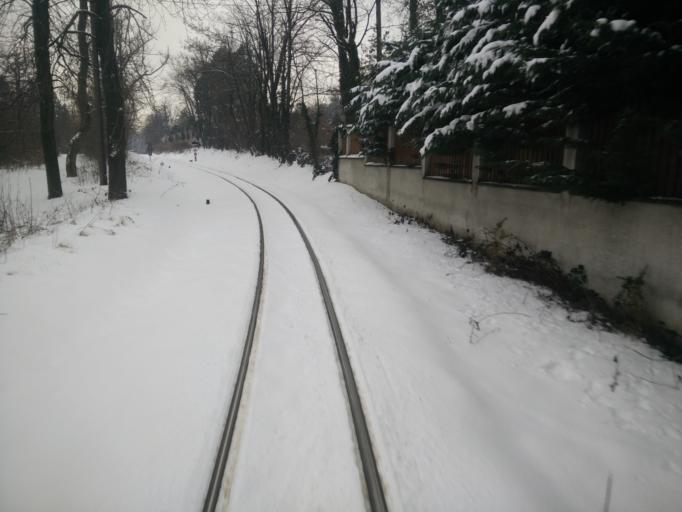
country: HU
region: Pest
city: Budaors
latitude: 47.5002
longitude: 18.9652
